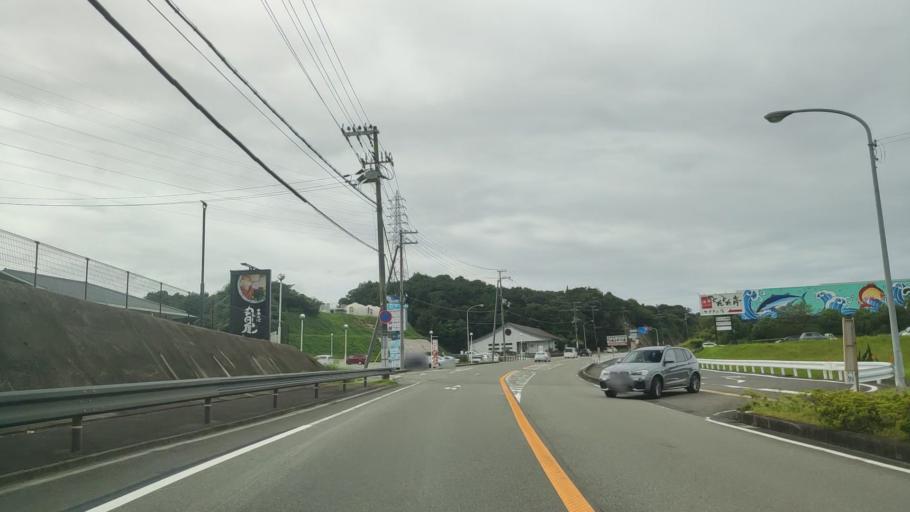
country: JP
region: Wakayama
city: Tanabe
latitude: 33.6816
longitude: 135.3774
